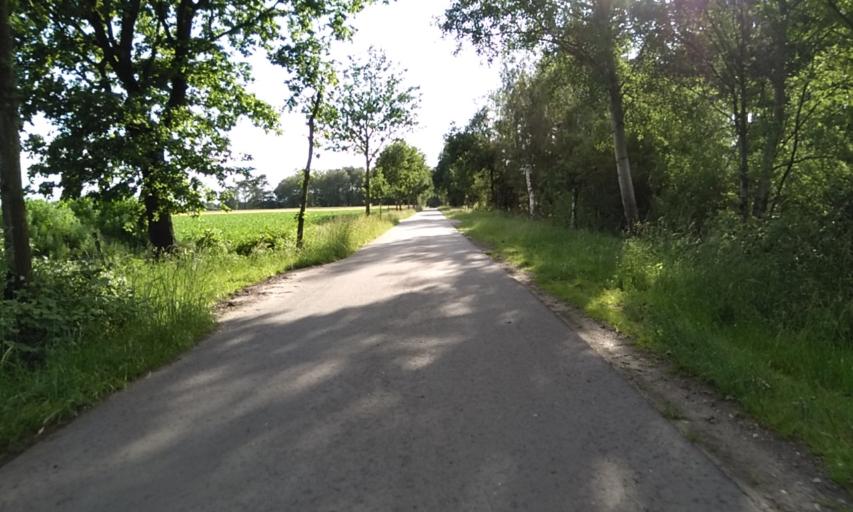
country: DE
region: Lower Saxony
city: Ahlerstedt
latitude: 53.3610
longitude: 9.4588
